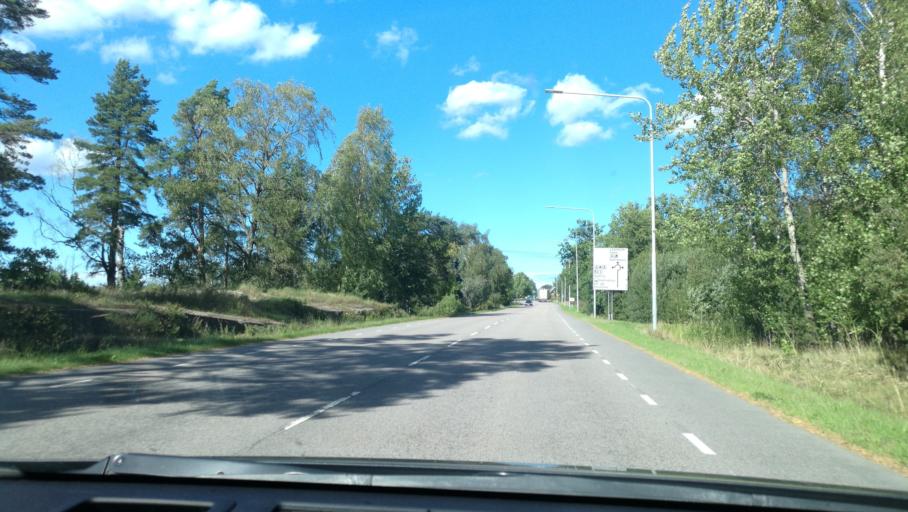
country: SE
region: Vaestra Goetaland
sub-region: Mariestads Kommun
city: Mariestad
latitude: 58.6896
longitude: 13.8428
